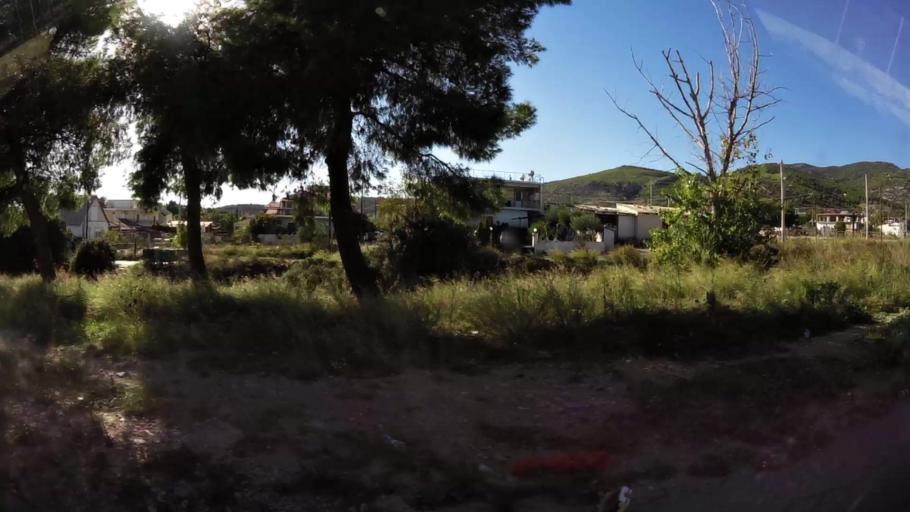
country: GR
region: Attica
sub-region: Nomarchia Anatolikis Attikis
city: Acharnes
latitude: 38.1024
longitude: 23.7237
